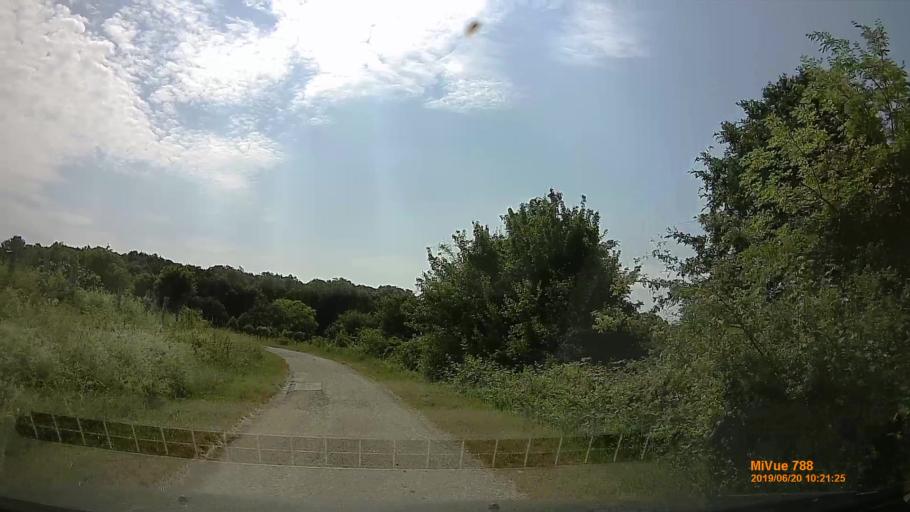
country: HU
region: Baranya
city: Mecseknadasd
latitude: 46.2094
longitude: 18.4762
